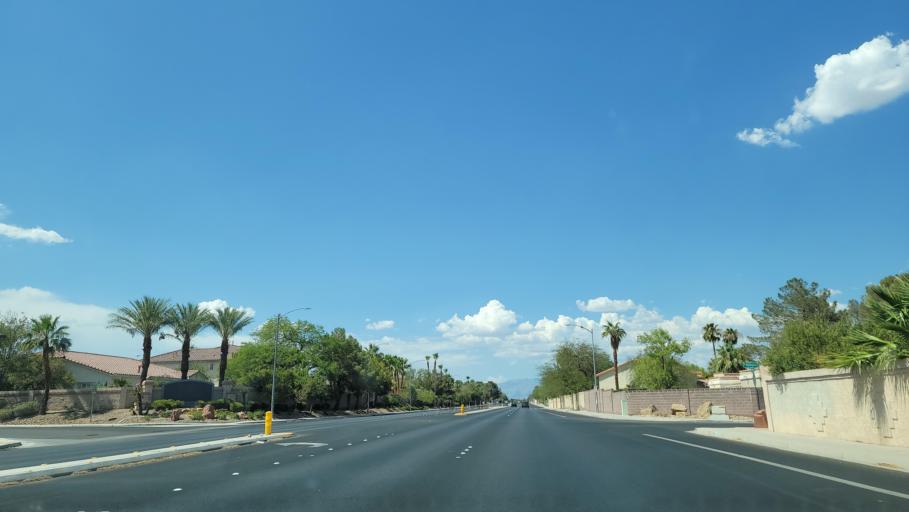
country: US
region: Nevada
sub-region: Clark County
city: Spring Valley
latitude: 36.1323
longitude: -115.2609
